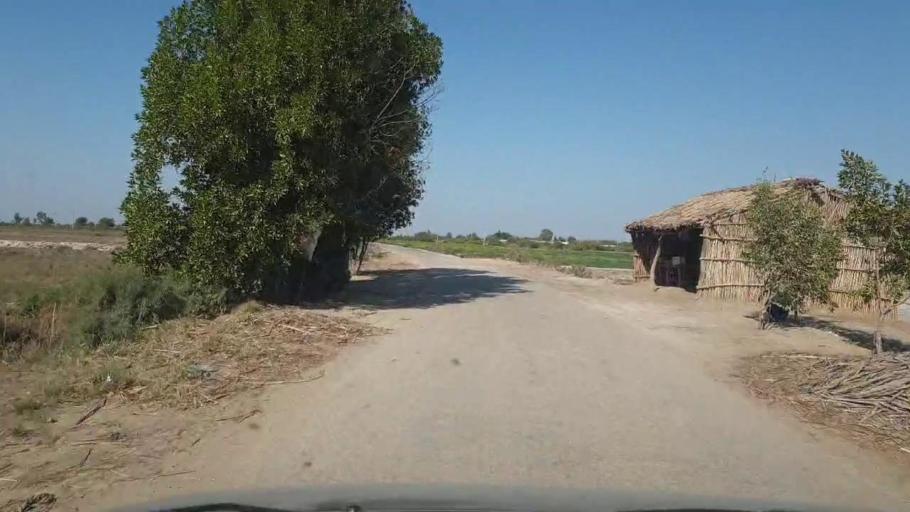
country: PK
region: Sindh
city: Samaro
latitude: 25.3600
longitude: 69.3187
